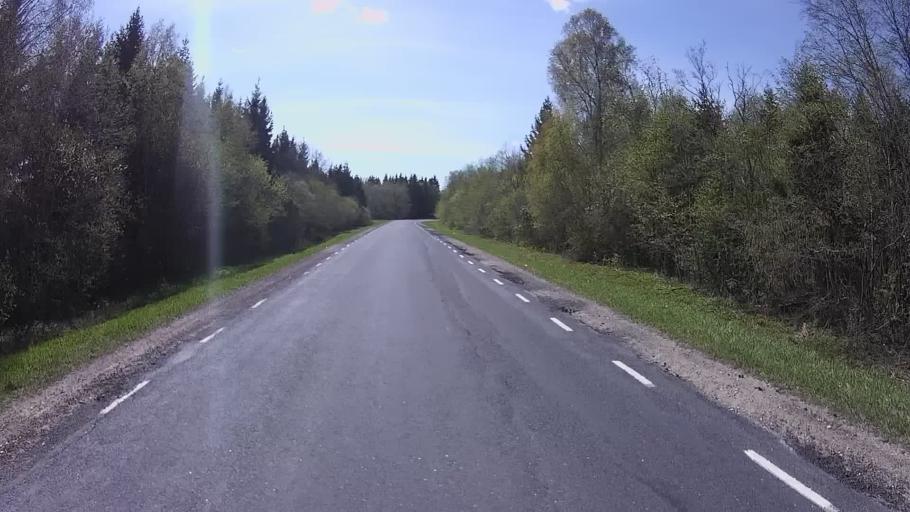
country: EE
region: Laeaene
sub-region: Ridala Parish
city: Uuemoisa
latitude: 59.0088
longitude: 23.7820
